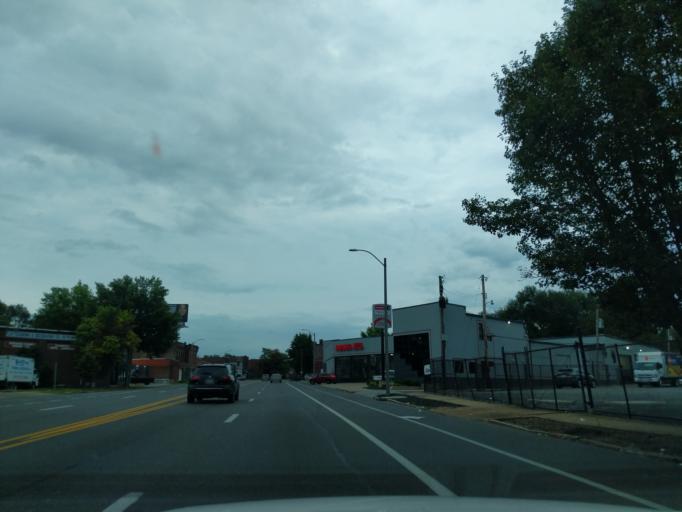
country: US
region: Missouri
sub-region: City of Saint Louis
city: St. Louis
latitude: 38.6056
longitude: -90.2222
